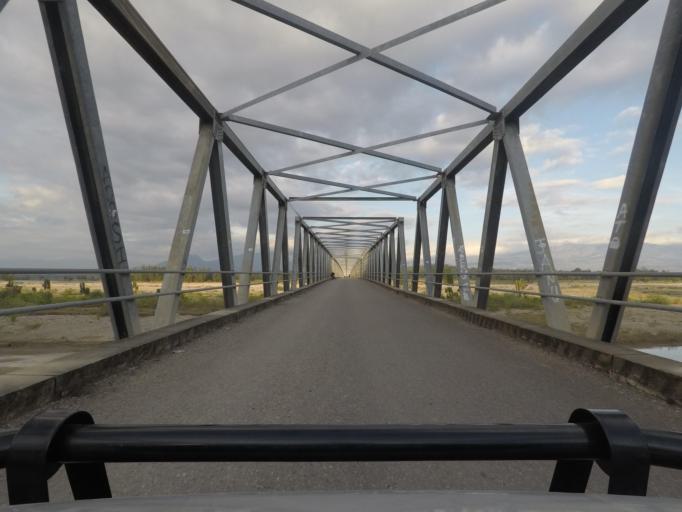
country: TL
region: Bobonaro
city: Maliana
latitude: -8.9606
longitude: 125.1106
